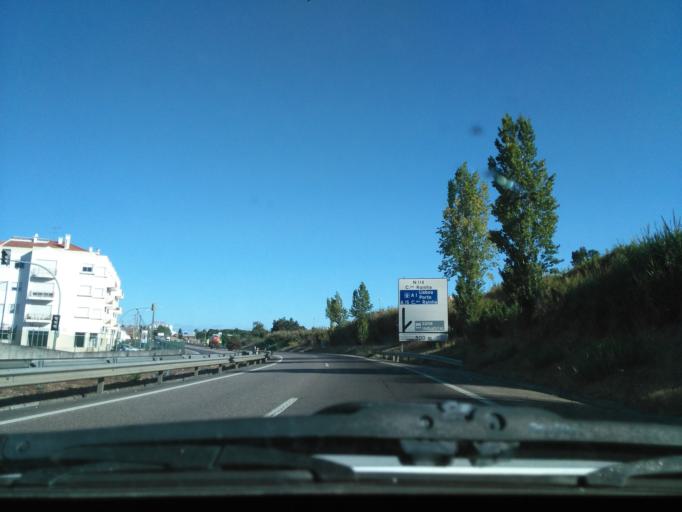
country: PT
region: Santarem
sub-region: Santarem
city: Santarem
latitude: 39.2550
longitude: -8.6986
